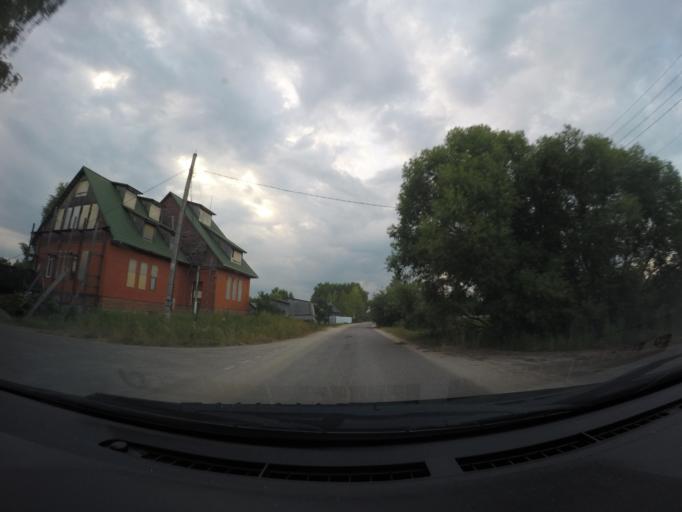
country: RU
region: Moskovskaya
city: Krasnyy Tkach
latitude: 55.3837
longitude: 39.2039
